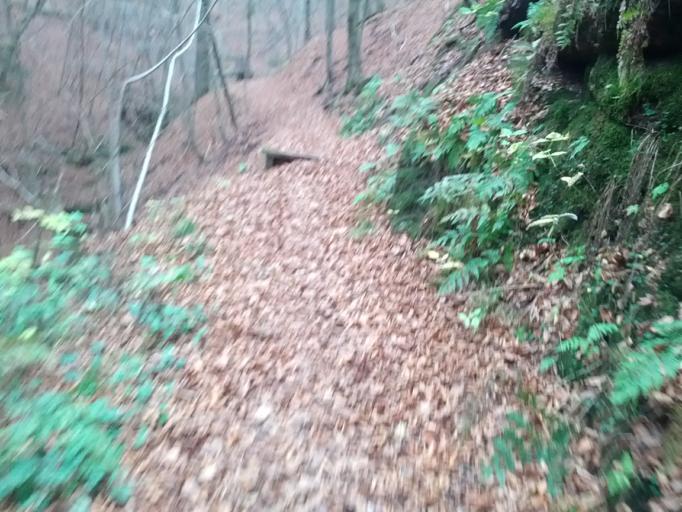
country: DE
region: Thuringia
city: Eisenach
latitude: 50.9480
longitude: 10.3196
